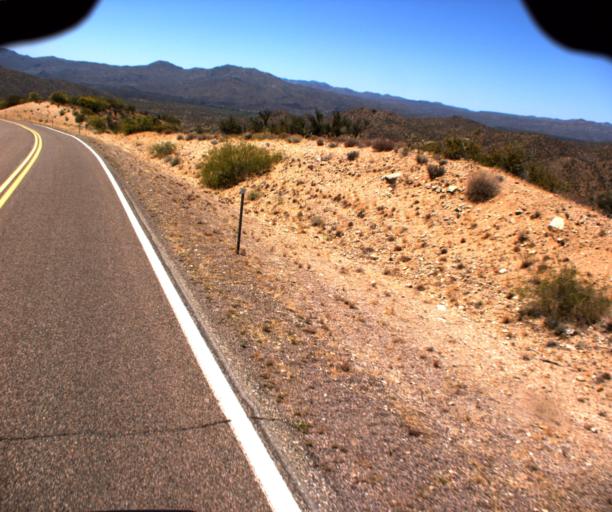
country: US
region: Arizona
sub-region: Yavapai County
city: Bagdad
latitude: 34.4614
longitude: -113.0000
